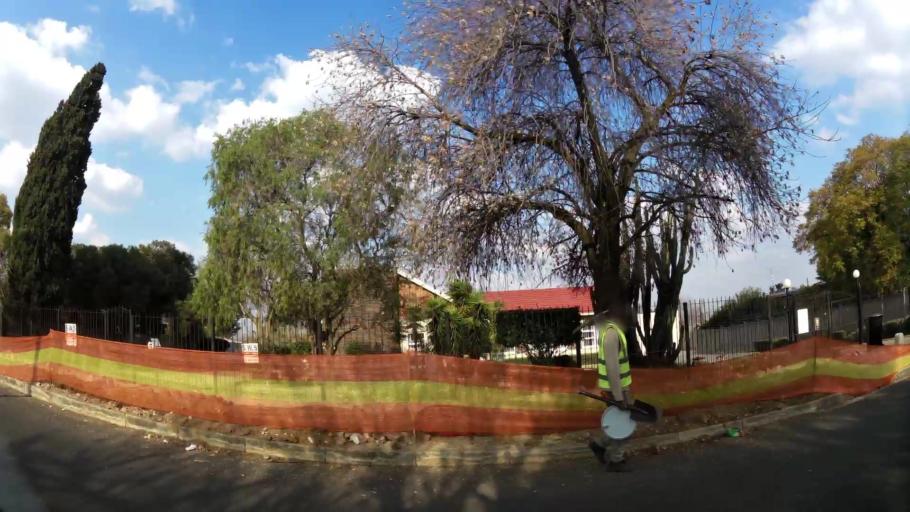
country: ZA
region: Gauteng
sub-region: Ekurhuleni Metropolitan Municipality
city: Germiston
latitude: -26.2448
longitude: 28.1841
